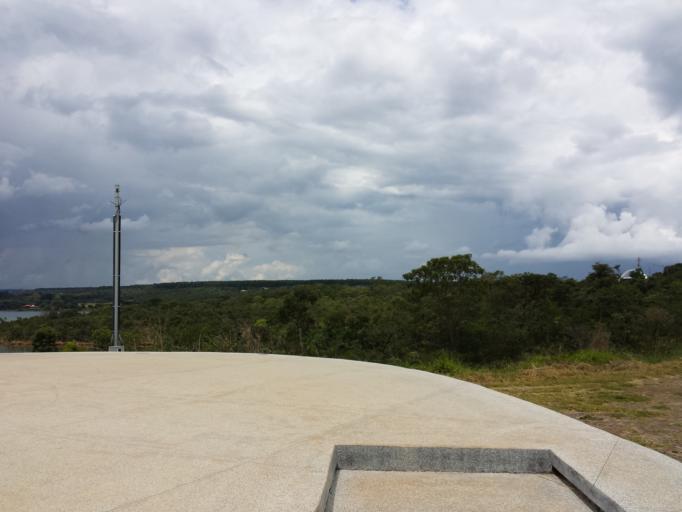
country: BR
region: Federal District
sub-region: Brasilia
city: Brasilia
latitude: -15.7975
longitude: -47.8105
